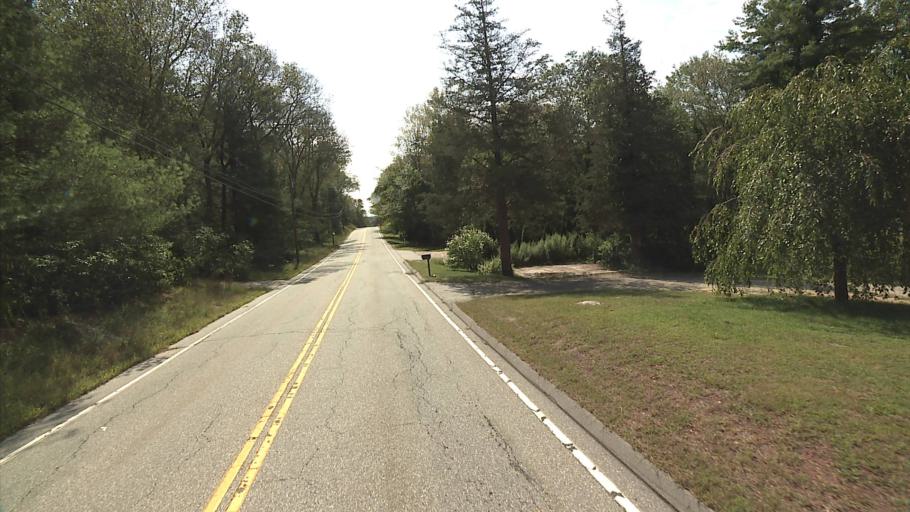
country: US
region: Connecticut
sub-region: Windham County
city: Plainfield Village
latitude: 41.6853
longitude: -71.9672
